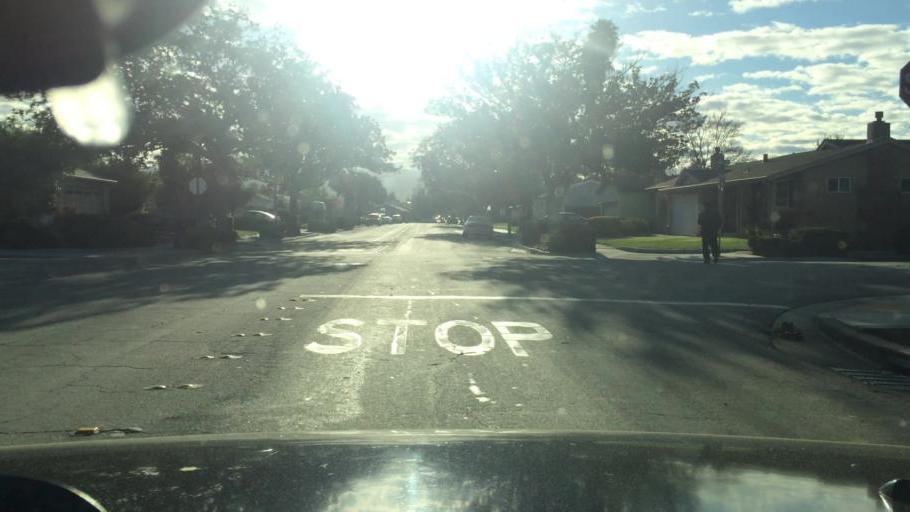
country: US
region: California
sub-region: Alameda County
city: Fremont
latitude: 37.5470
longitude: -121.9936
